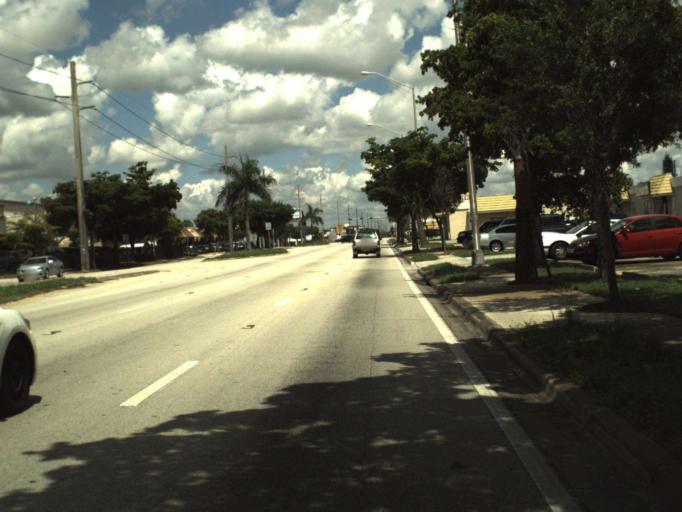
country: US
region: Florida
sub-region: Miami-Dade County
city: Golden Glades
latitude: 25.9035
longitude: -80.2114
